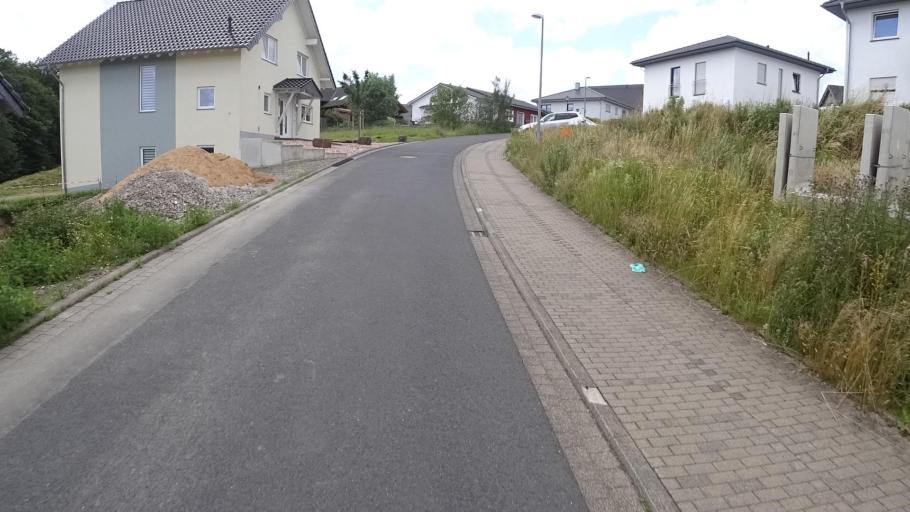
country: DE
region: Rheinland-Pfalz
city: Vettelschoss
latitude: 50.6175
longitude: 7.3235
